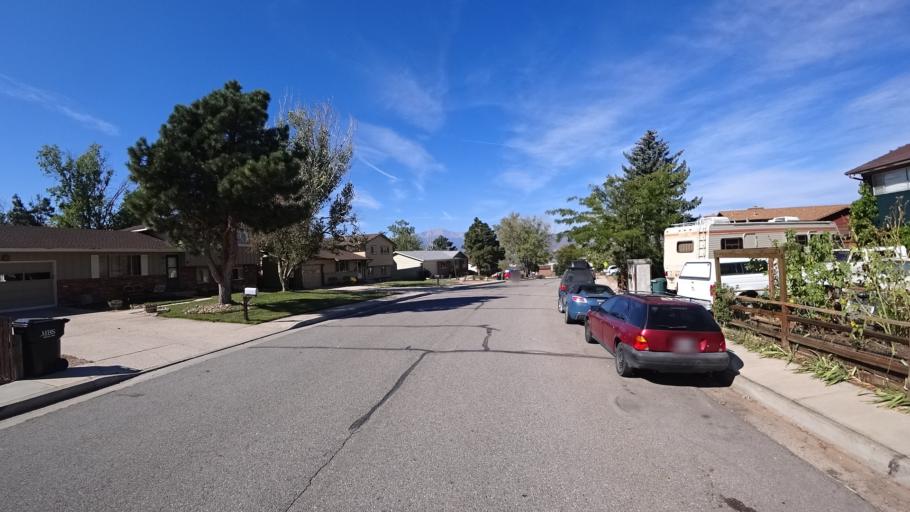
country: US
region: Colorado
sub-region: El Paso County
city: Cimarron Hills
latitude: 38.9208
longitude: -104.7678
